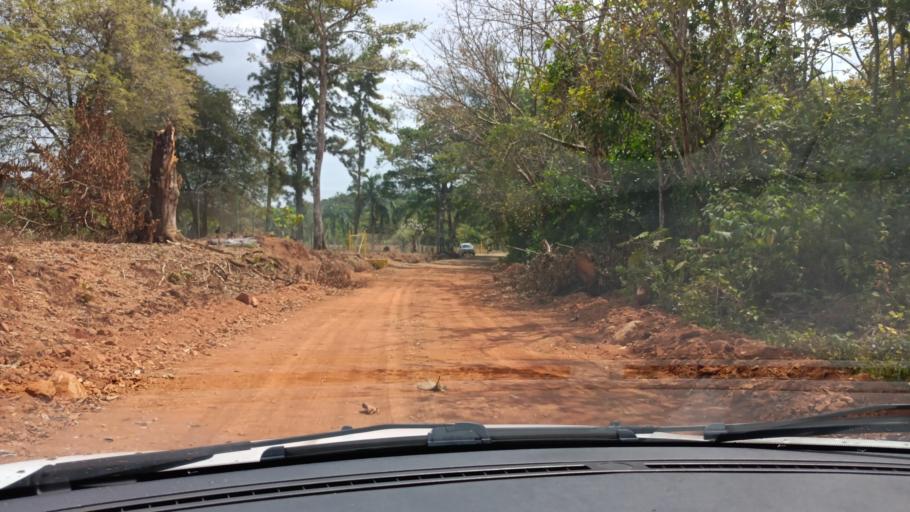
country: PA
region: Panama
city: La Cabima
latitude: 9.1298
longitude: -79.4989
